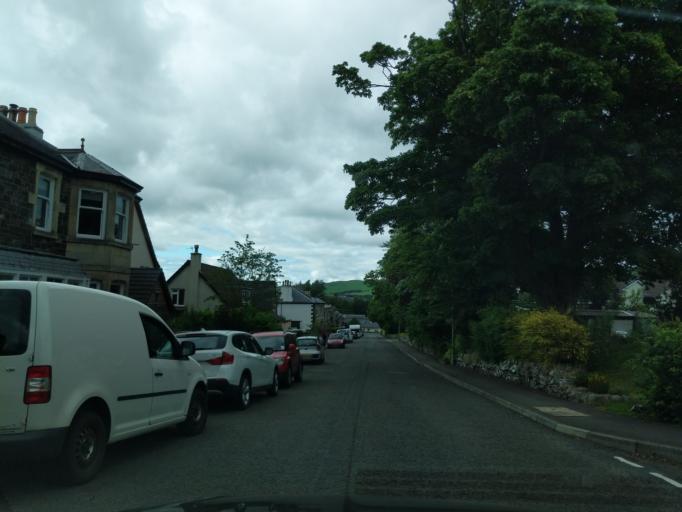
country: GB
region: Scotland
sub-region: The Scottish Borders
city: Peebles
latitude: 55.6473
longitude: -3.1989
